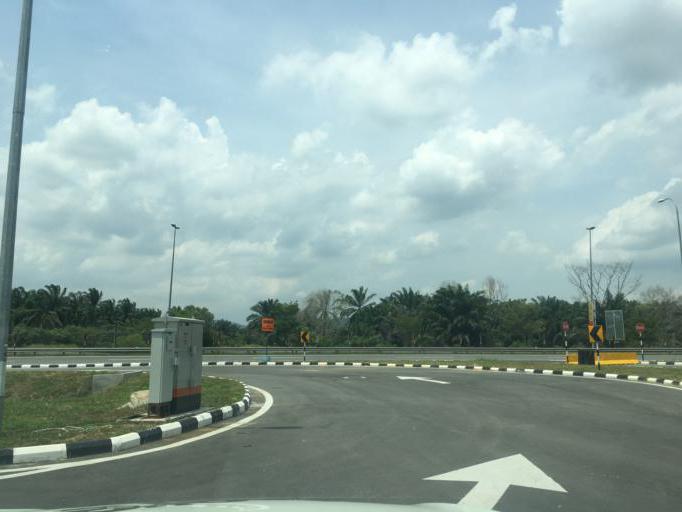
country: MY
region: Putrajaya
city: Putrajaya
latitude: 2.8565
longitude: 101.6942
